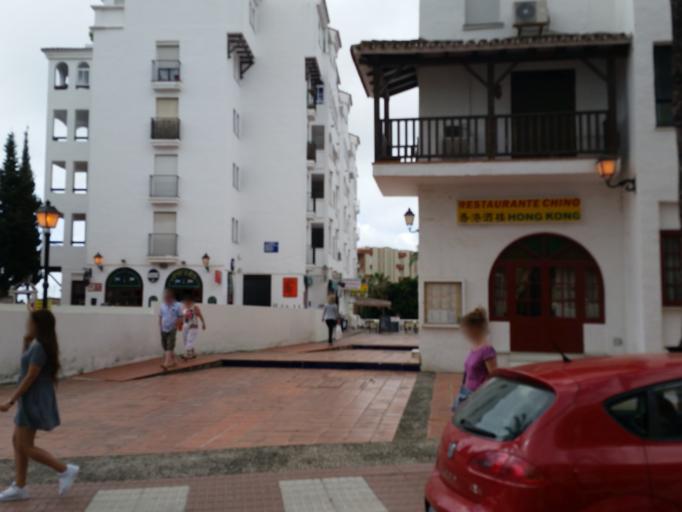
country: ES
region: Andalusia
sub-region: Provincia de Malaga
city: Torremolinos
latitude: 36.5966
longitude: -4.5255
